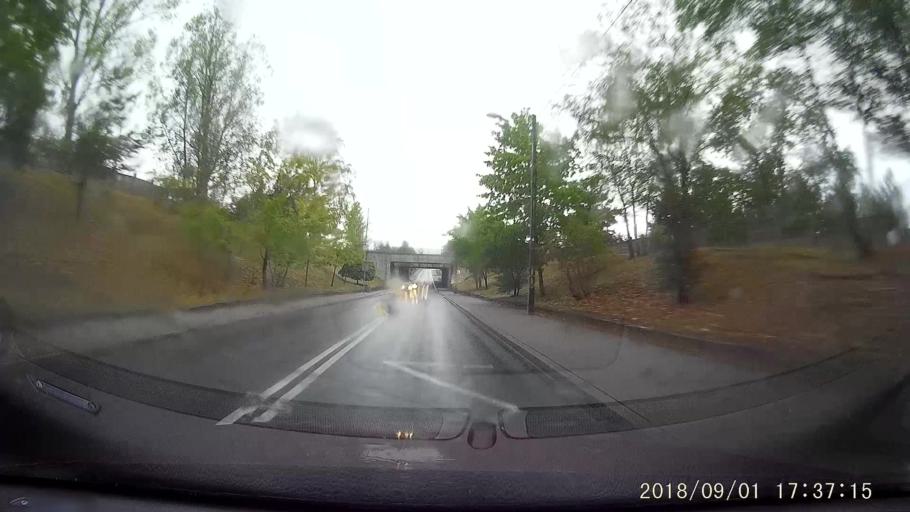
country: PL
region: Lubusz
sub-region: Powiat zaganski
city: Zagan
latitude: 51.6090
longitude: 15.3017
